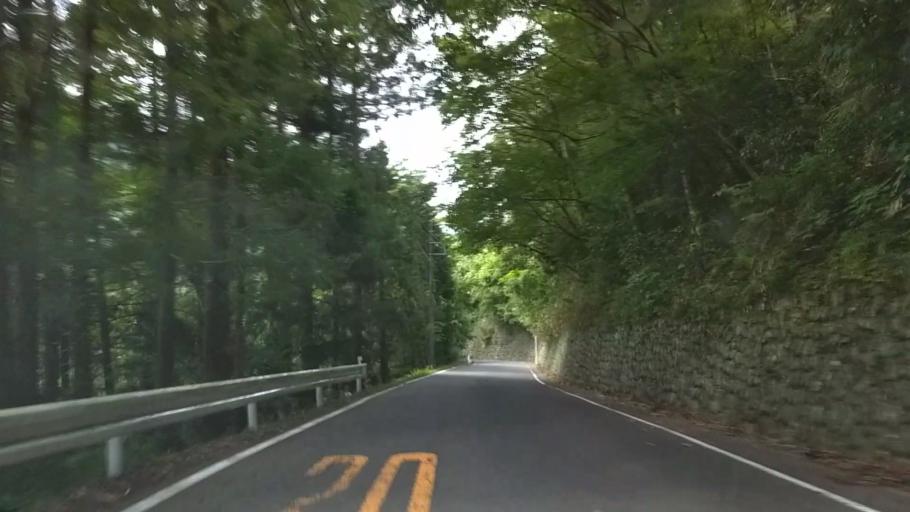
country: JP
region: Yamanashi
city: Uenohara
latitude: 35.5525
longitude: 139.1393
